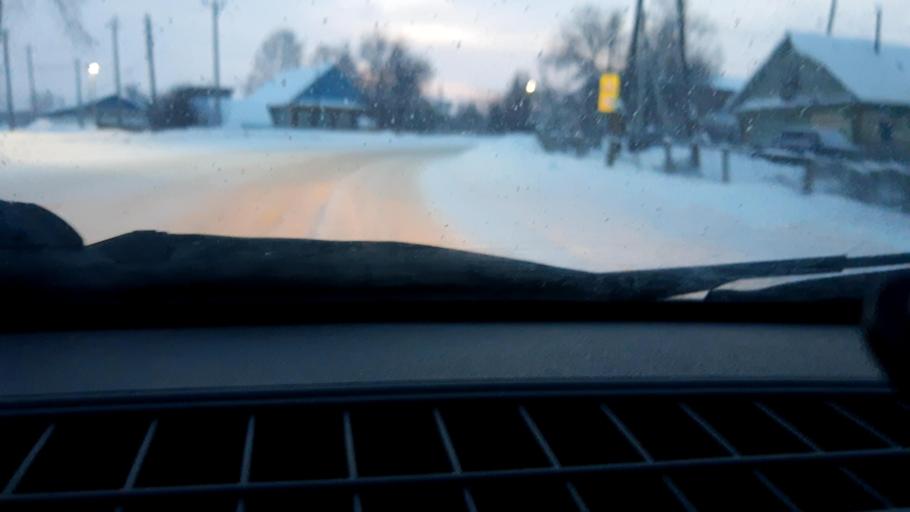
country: RU
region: Bashkortostan
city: Davlekanovo
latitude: 54.5793
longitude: 54.9371
